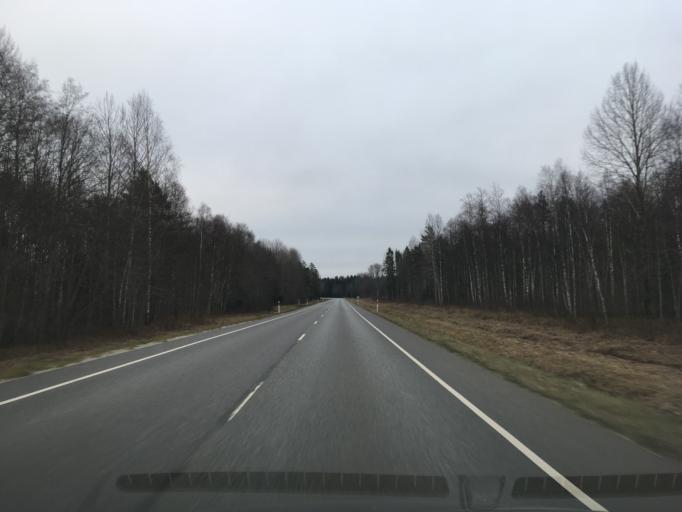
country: EE
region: Laeaene-Virumaa
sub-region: Kadrina vald
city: Kadrina
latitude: 59.4495
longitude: 26.0561
